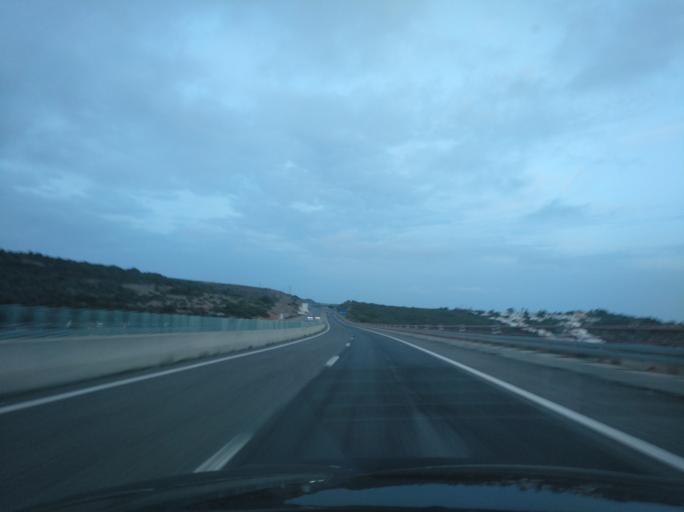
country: PT
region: Faro
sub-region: Lagos
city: Lagos
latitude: 37.1435
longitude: -8.7107
